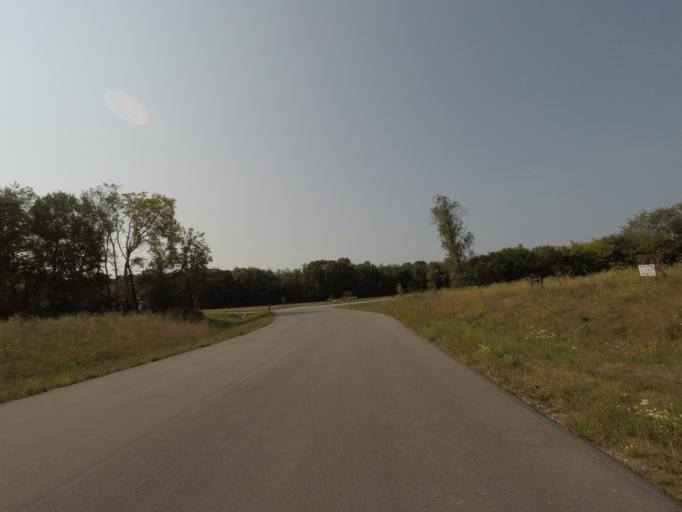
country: US
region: Wisconsin
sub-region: Waukesha County
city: Delafield
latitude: 43.0302
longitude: -88.4166
